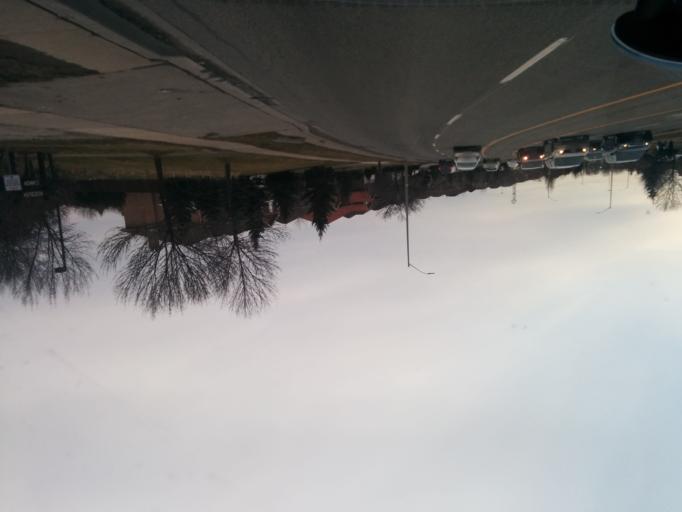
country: CA
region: Ontario
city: Mississauga
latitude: 43.5762
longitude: -79.6831
